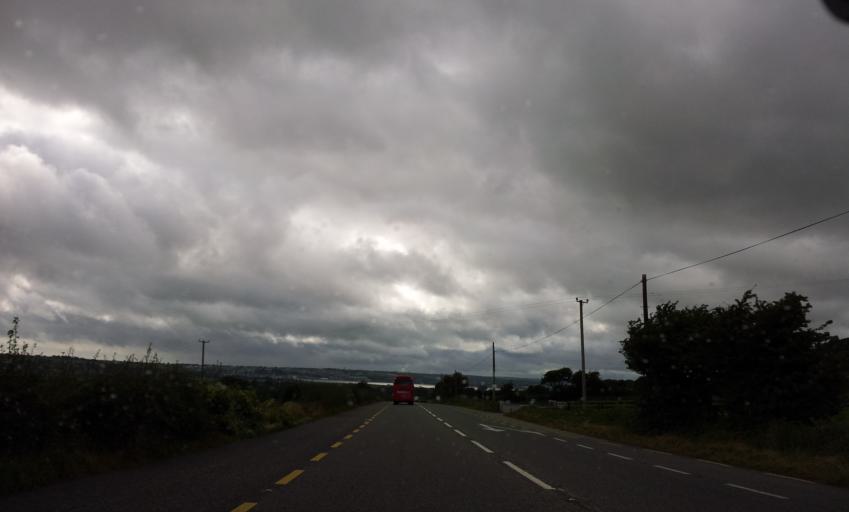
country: IE
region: Munster
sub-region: County Cork
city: Youghal
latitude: 51.9744
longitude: -7.7682
